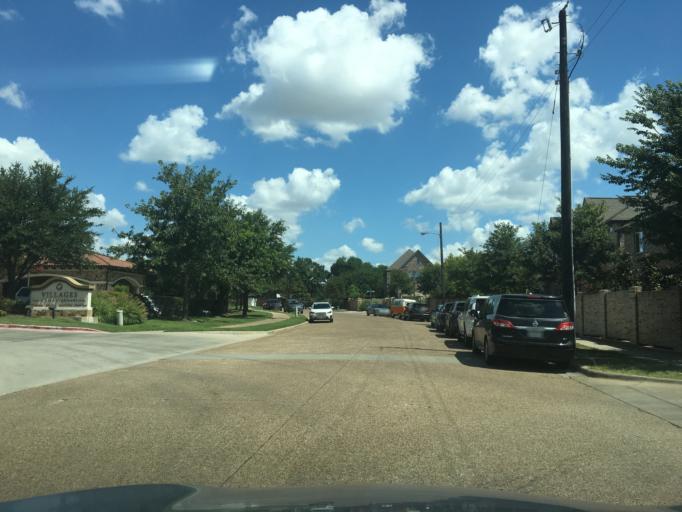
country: US
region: Texas
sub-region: Dallas County
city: Garland
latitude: 32.8659
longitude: -96.7039
